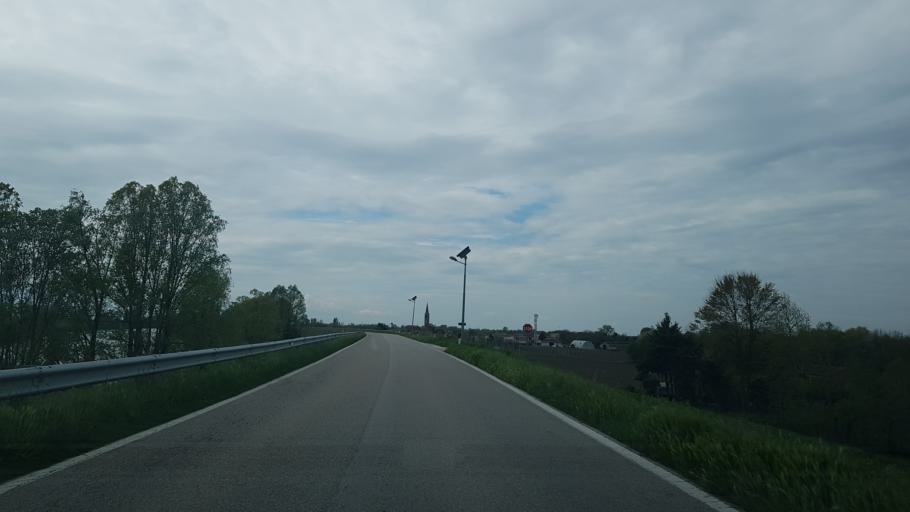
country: IT
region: Veneto
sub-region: Provincia di Rovigo
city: Lusia
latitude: 45.1104
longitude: 11.6293
